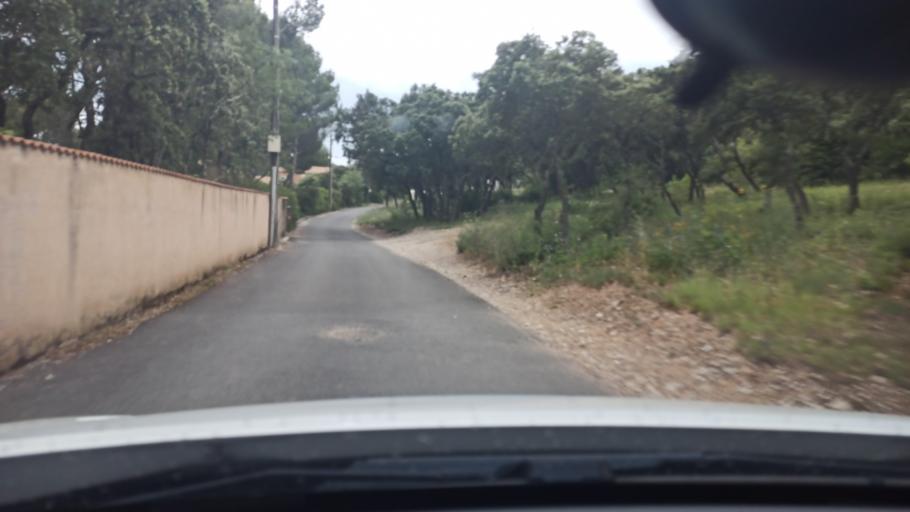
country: FR
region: Languedoc-Roussillon
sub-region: Departement du Gard
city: Les Angles
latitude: 43.9713
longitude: 4.7670
